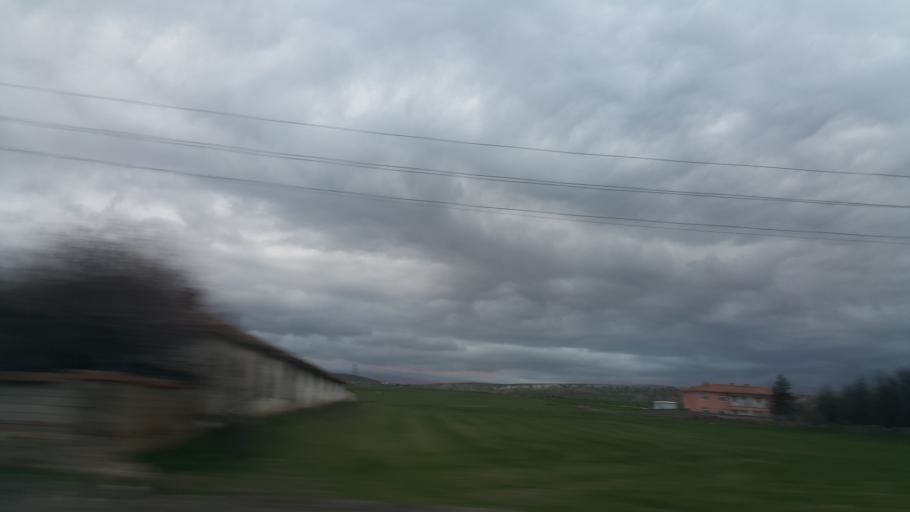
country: TR
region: Ankara
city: Ikizce
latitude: 39.4821
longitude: 32.8692
